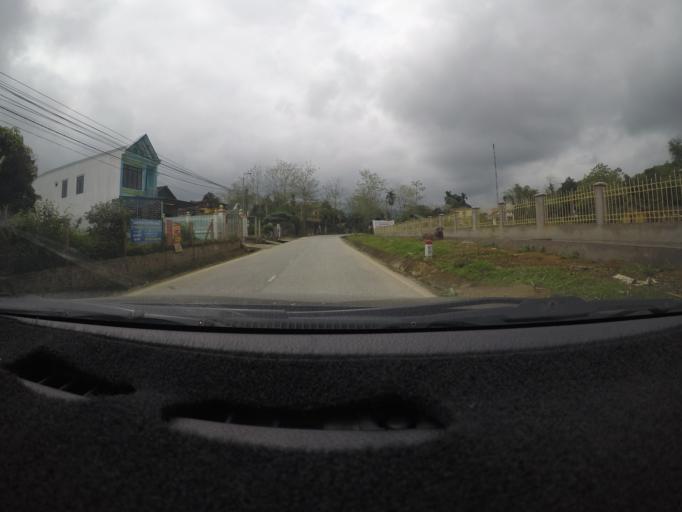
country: VN
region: Yen Bai
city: Co Phuc
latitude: 21.8864
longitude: 104.8344
